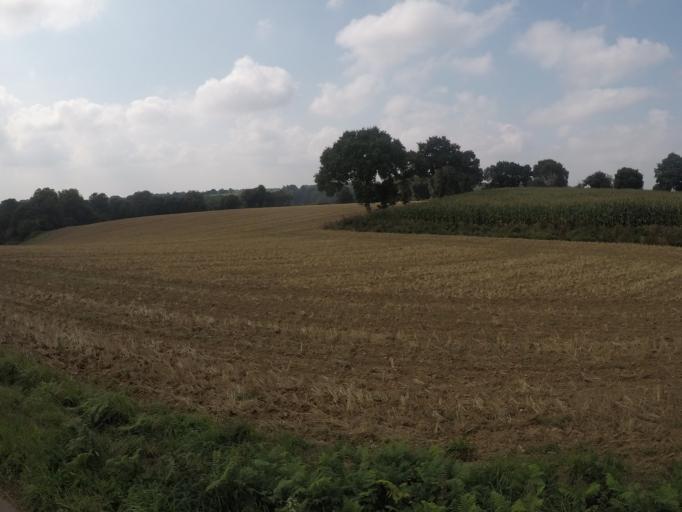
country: FR
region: Brittany
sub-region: Departement des Cotes-d'Armor
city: Plelo
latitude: 48.5609
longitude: -2.9532
